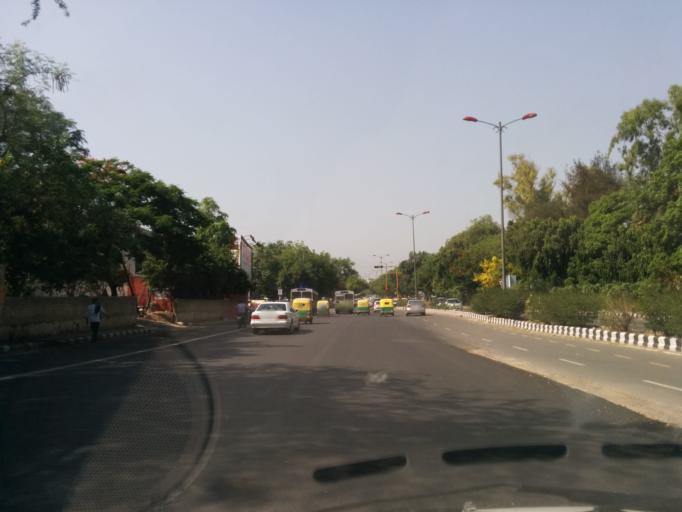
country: IN
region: NCT
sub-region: New Delhi
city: New Delhi
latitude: 28.5547
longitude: 77.2058
